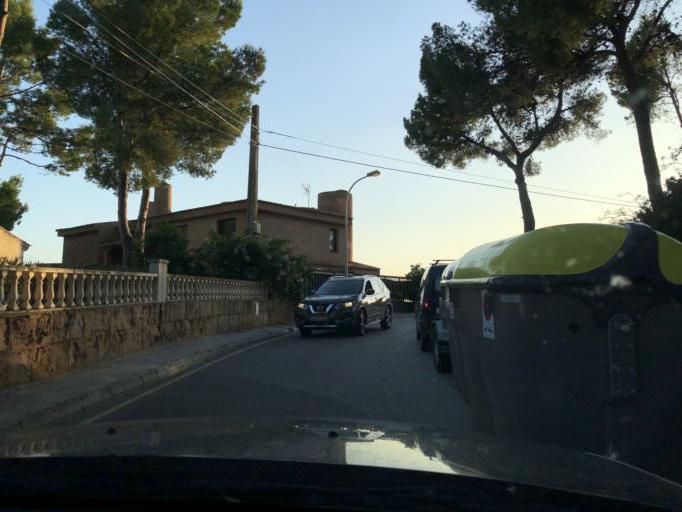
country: ES
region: Balearic Islands
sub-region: Illes Balears
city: Santa Ponsa
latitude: 39.5278
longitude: 2.4740
